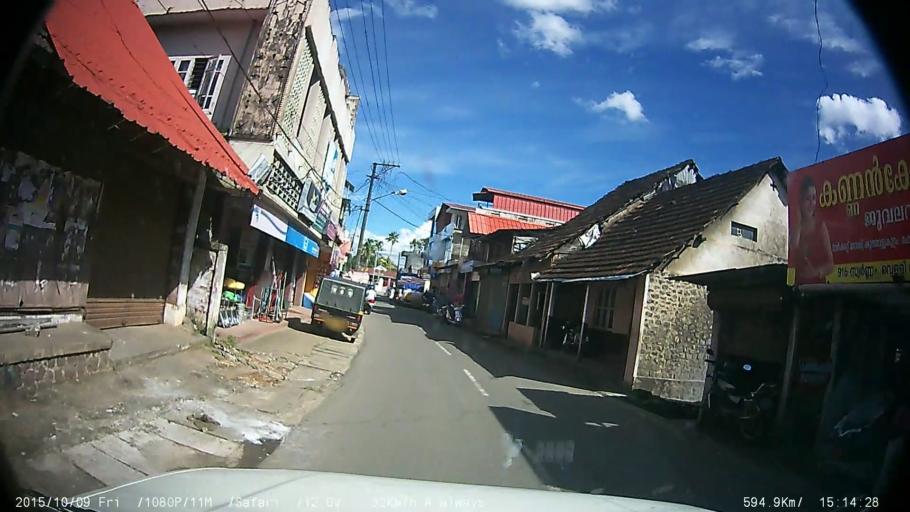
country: IN
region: Kerala
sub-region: Ernakulam
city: Piravam
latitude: 9.8623
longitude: 76.5944
